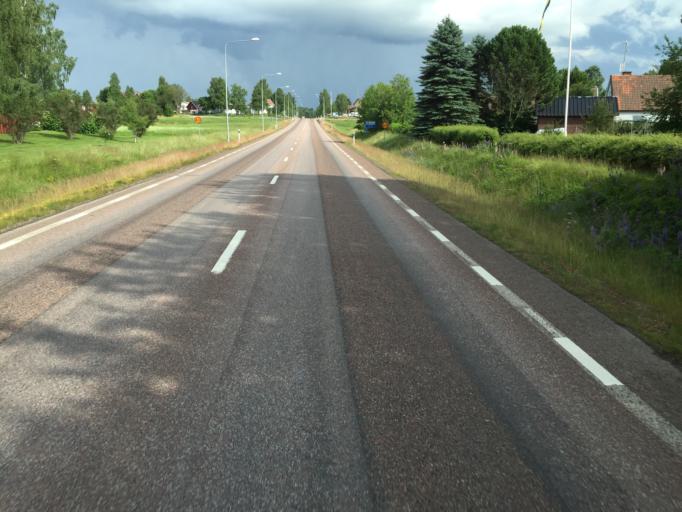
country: SE
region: Dalarna
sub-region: Vansbro Kommun
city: Jarna
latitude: 60.5505
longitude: 14.3607
